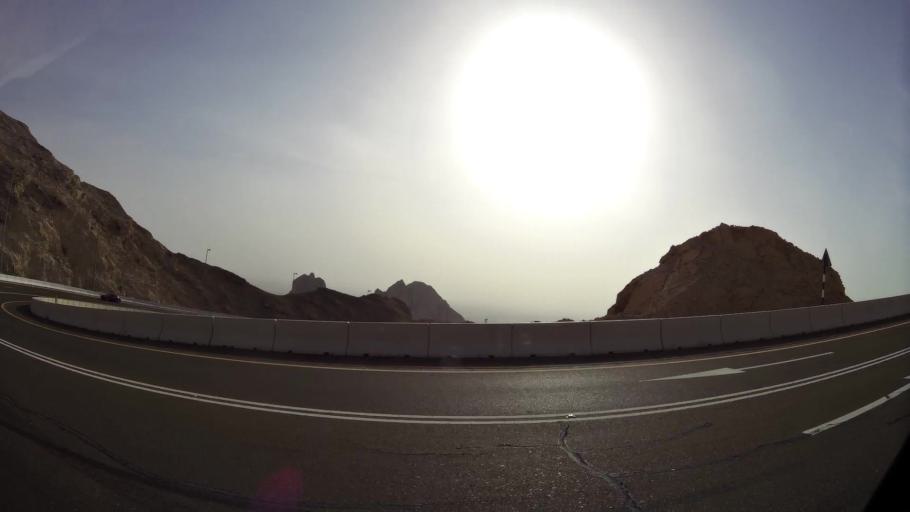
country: AE
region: Abu Dhabi
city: Al Ain
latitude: 24.0949
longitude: 55.7598
